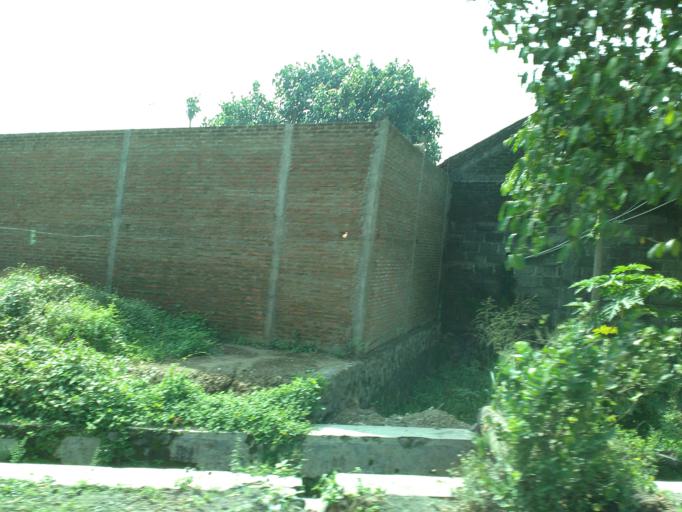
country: ID
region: Central Java
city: Jogonalan
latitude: -7.7323
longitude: 110.5445
